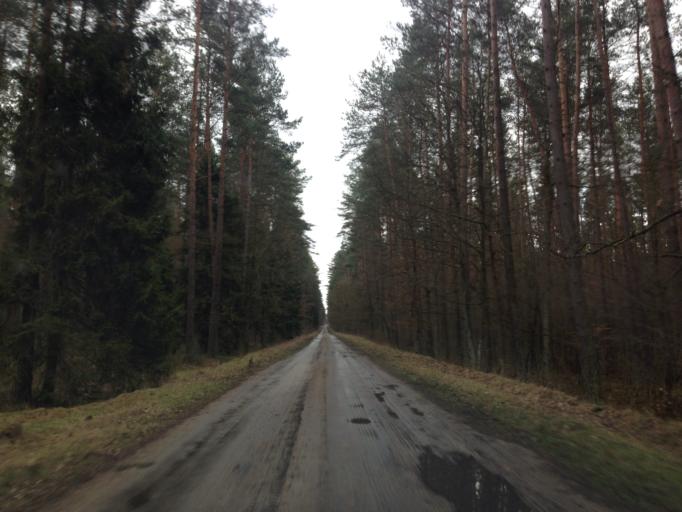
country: PL
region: Kujawsko-Pomorskie
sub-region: Powiat brodnicki
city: Gorzno
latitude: 53.1823
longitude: 19.7014
